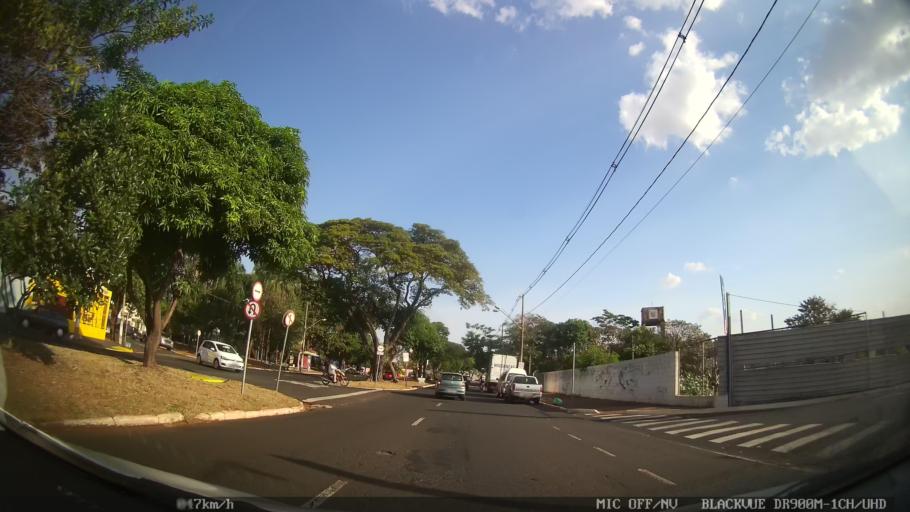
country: BR
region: Sao Paulo
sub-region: Ribeirao Preto
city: Ribeirao Preto
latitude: -21.1568
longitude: -47.8068
